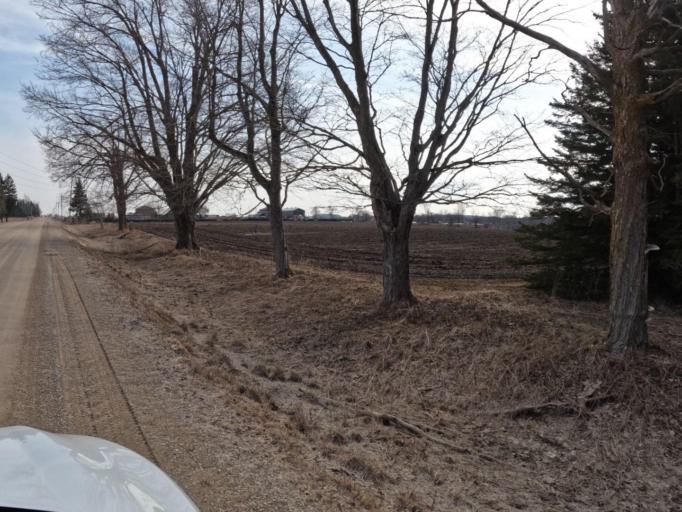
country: CA
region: Ontario
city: Orangeville
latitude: 43.8862
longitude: -80.2982
